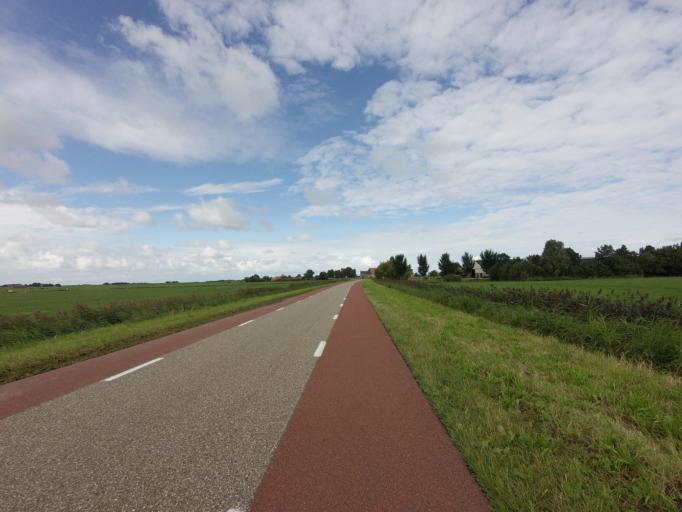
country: NL
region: Friesland
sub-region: Sudwest Fryslan
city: Workum
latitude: 53.0253
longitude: 5.4713
